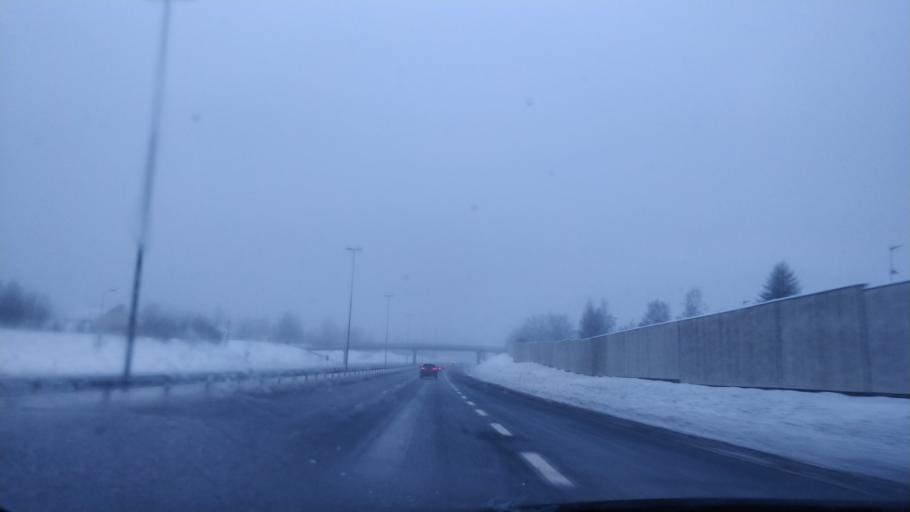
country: FI
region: Lapland
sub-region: Kemi-Tornio
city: Kemi
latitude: 65.7449
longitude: 24.5820
